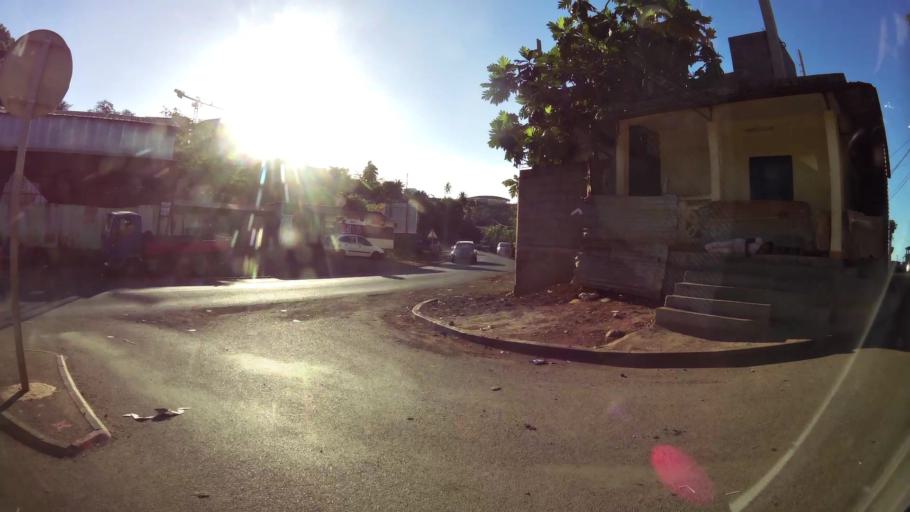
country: YT
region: Koungou
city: Koungou
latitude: -12.7358
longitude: 45.2053
